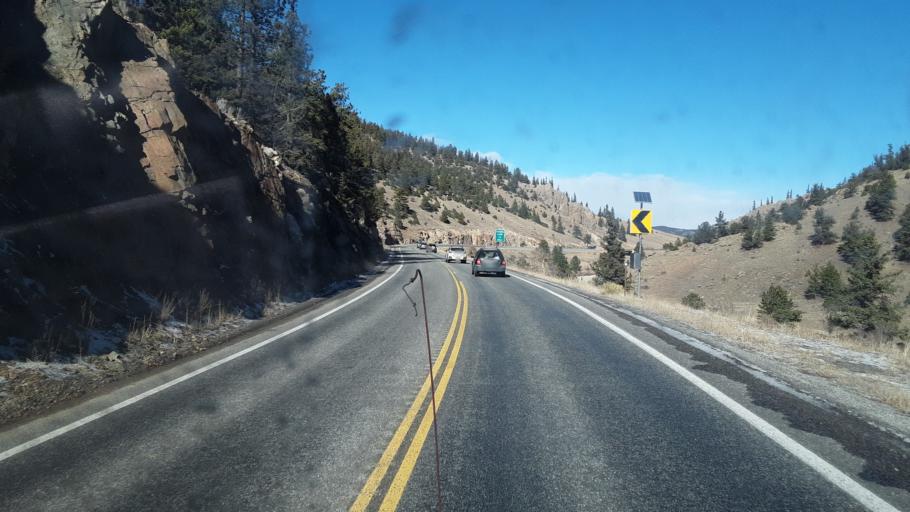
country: US
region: Colorado
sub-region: Chaffee County
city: Buena Vista
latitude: 38.8538
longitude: -105.9837
